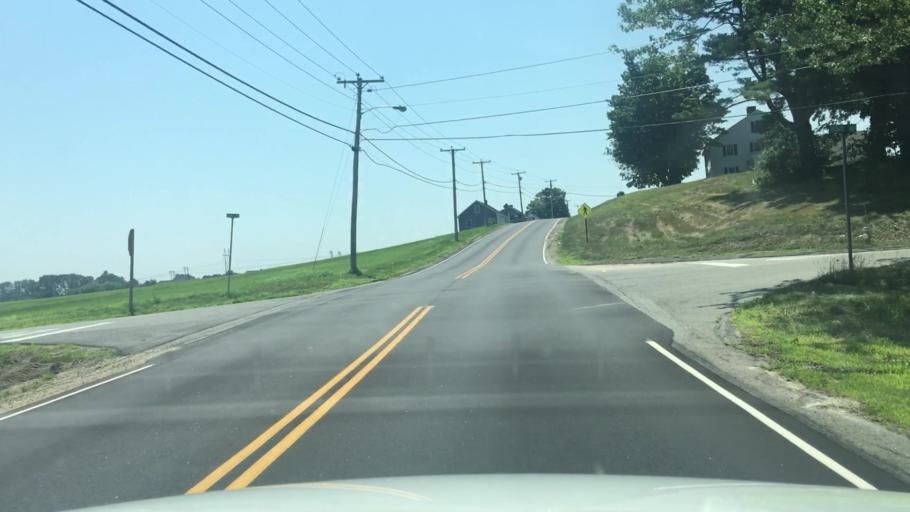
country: US
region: Maine
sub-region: Cumberland County
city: Cumberland Center
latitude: 43.7783
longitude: -70.2602
